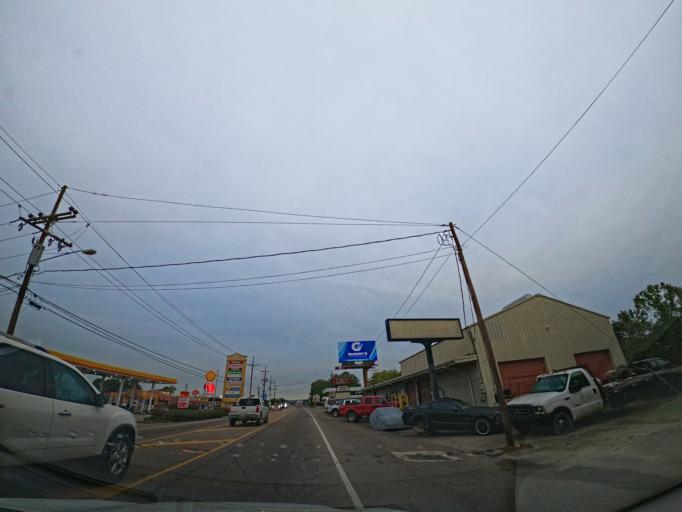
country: US
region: Louisiana
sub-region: Lafourche Parish
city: Mathews
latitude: 29.7046
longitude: -90.5660
